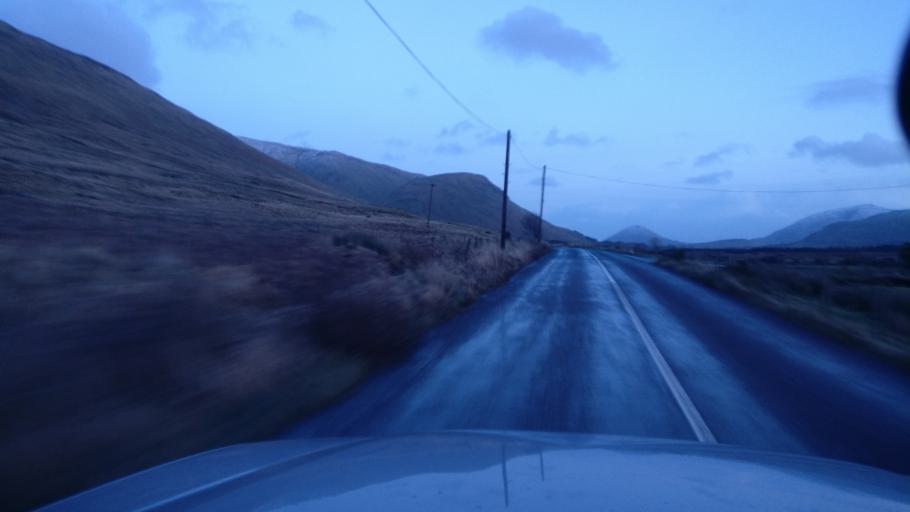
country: IE
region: Connaught
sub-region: Maigh Eo
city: Westport
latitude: 53.5590
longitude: -9.6475
